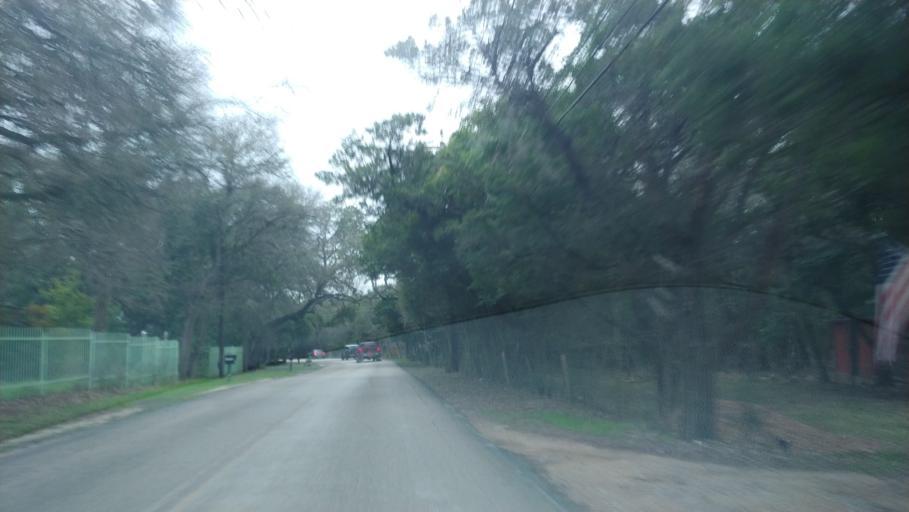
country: US
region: Texas
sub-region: Bexar County
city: Cross Mountain
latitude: 29.6261
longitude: -98.6835
